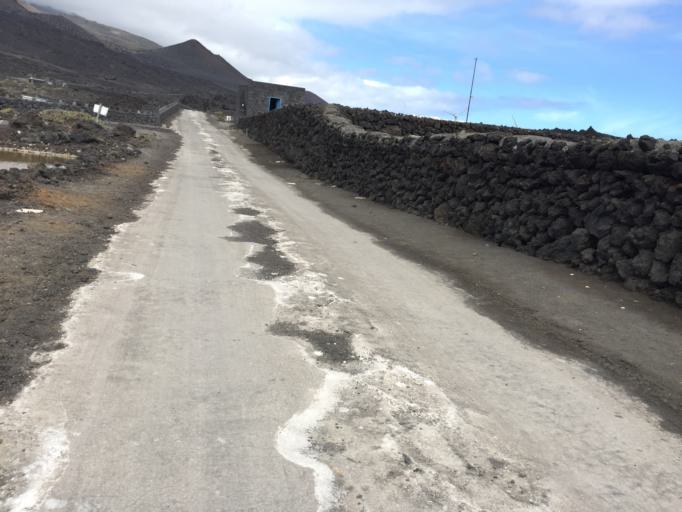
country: ES
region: Canary Islands
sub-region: Provincia de Santa Cruz de Tenerife
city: Fuencaliente de la Palma
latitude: 28.4546
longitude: -17.8416
